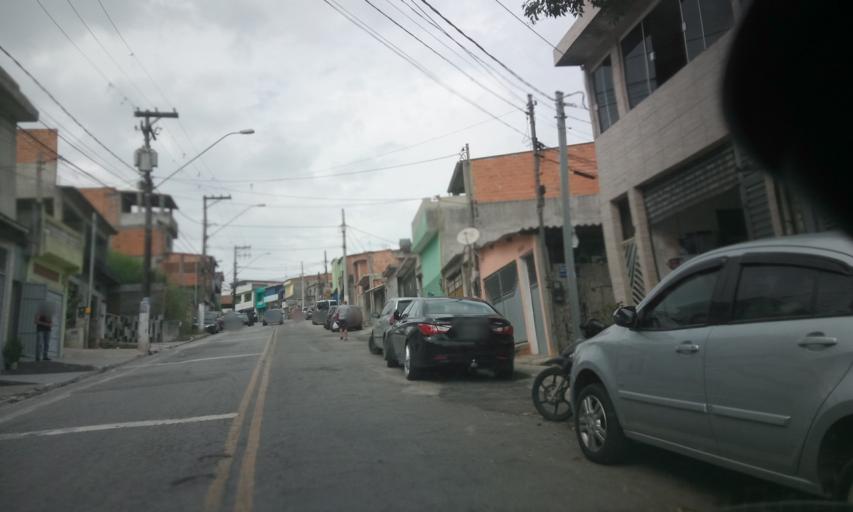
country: BR
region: Sao Paulo
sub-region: Sao Bernardo Do Campo
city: Sao Bernardo do Campo
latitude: -23.7716
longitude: -46.6013
